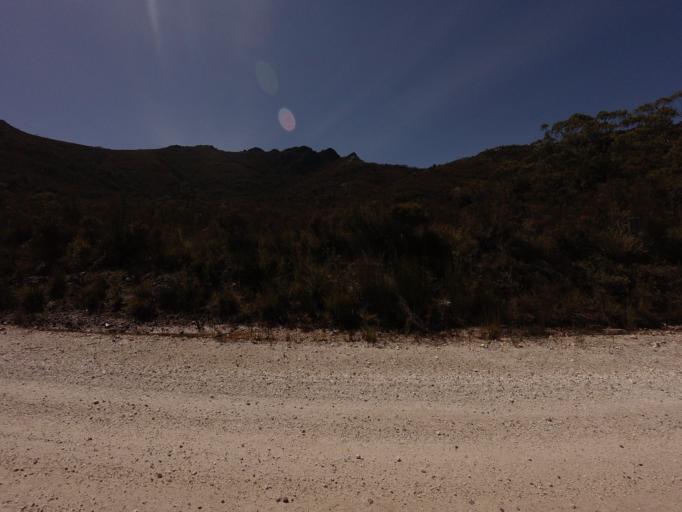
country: AU
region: Tasmania
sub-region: Huon Valley
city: Geeveston
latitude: -42.9379
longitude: 146.3481
